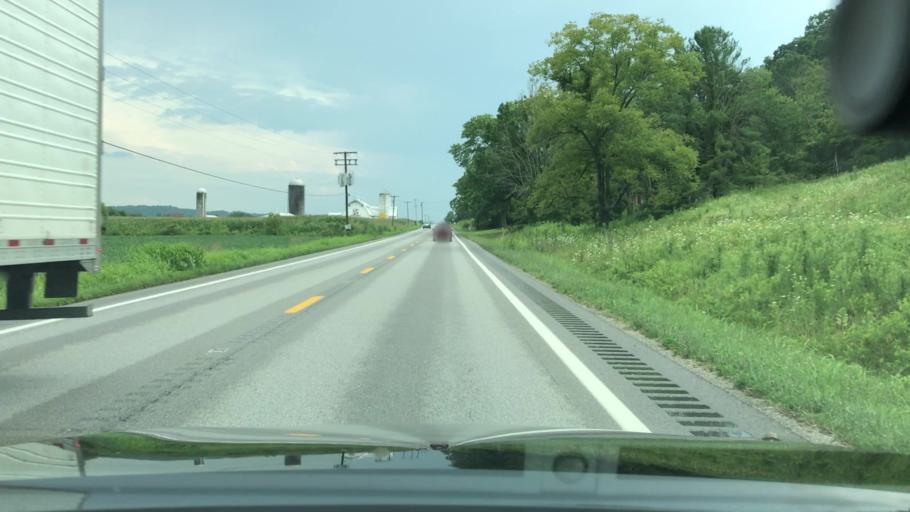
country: US
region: West Virginia
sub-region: Putnam County
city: Buffalo
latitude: 38.7306
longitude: -81.9732
